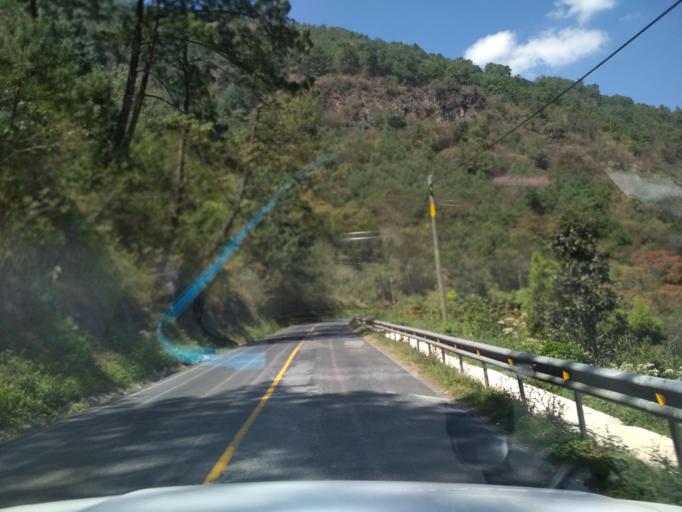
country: MX
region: Veracruz
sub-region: Tlilapan
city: Tonalixco
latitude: 18.7726
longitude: -97.0817
